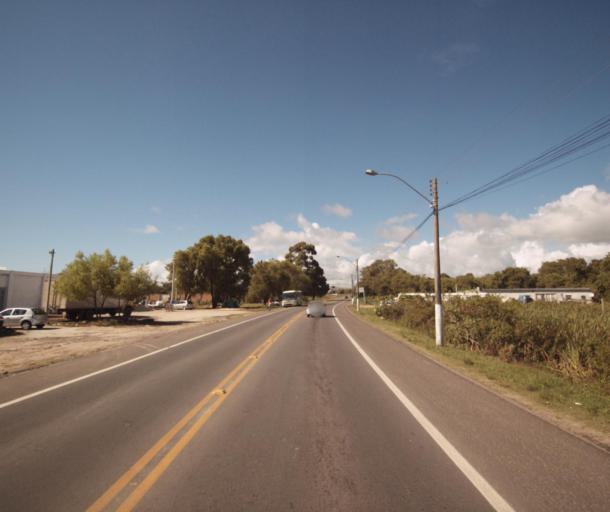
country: BR
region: Rio Grande do Sul
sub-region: Pelotas
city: Pelotas
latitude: -31.7594
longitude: -52.3562
